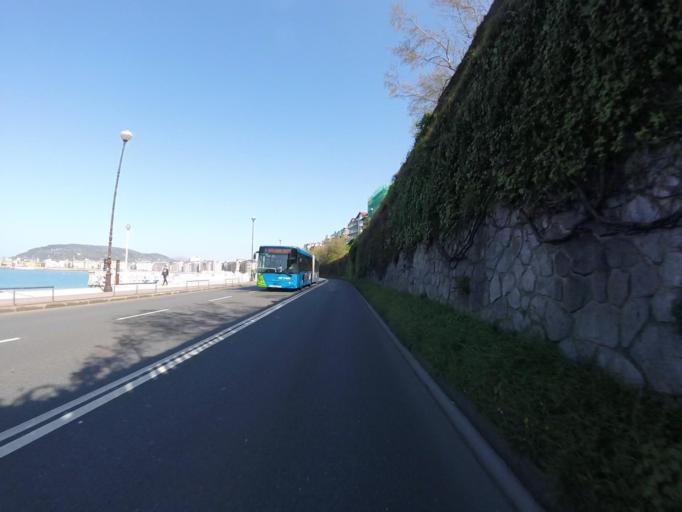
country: ES
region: Basque Country
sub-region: Provincia de Guipuzcoa
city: San Sebastian
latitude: 43.3146
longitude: -1.9967
